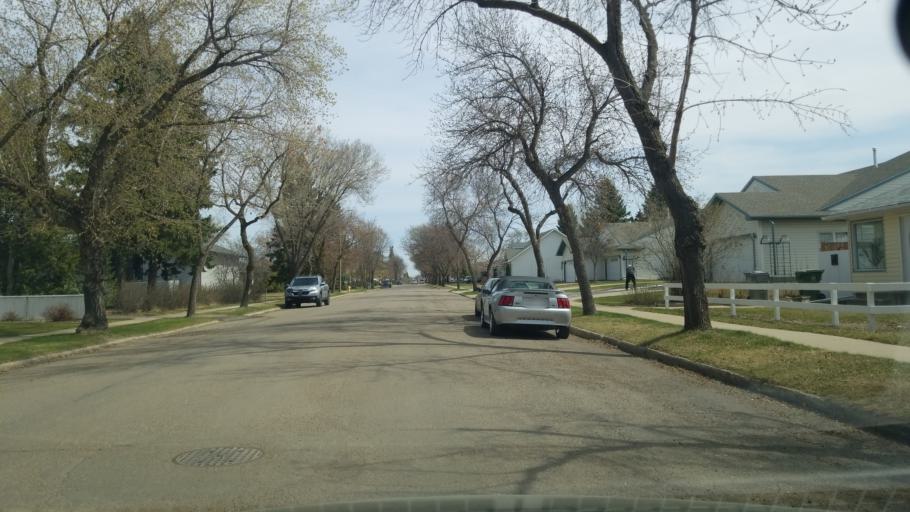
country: CA
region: Saskatchewan
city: Lloydminster
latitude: 53.2816
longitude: -110.0145
